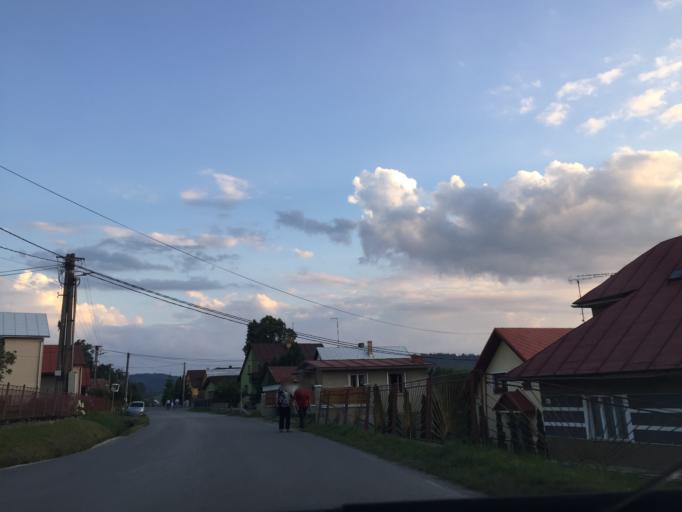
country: PL
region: Silesian Voivodeship
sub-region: Powiat zywiecki
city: Korbielow
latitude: 49.4770
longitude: 19.3828
